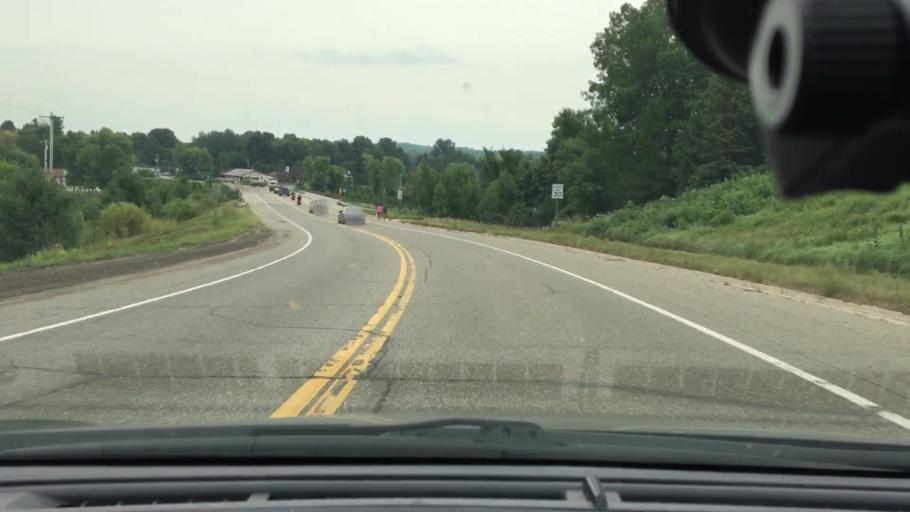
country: US
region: Minnesota
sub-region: Crow Wing County
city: Cross Lake
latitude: 46.8199
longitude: -93.9473
